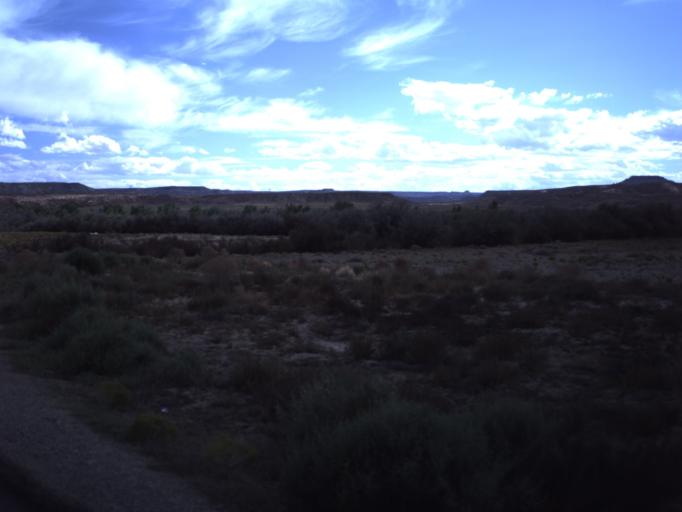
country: US
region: Utah
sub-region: San Juan County
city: Blanding
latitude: 37.2504
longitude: -109.2563
